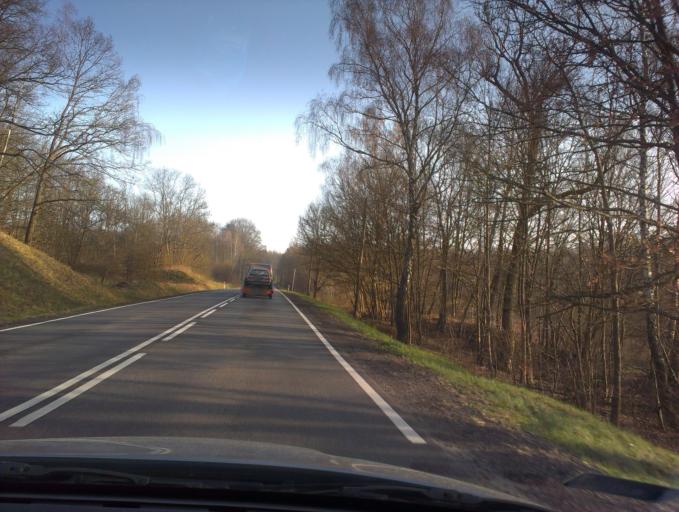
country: PL
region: West Pomeranian Voivodeship
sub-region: Powiat koszalinski
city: Bobolice
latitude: 53.8736
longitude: 16.6136
